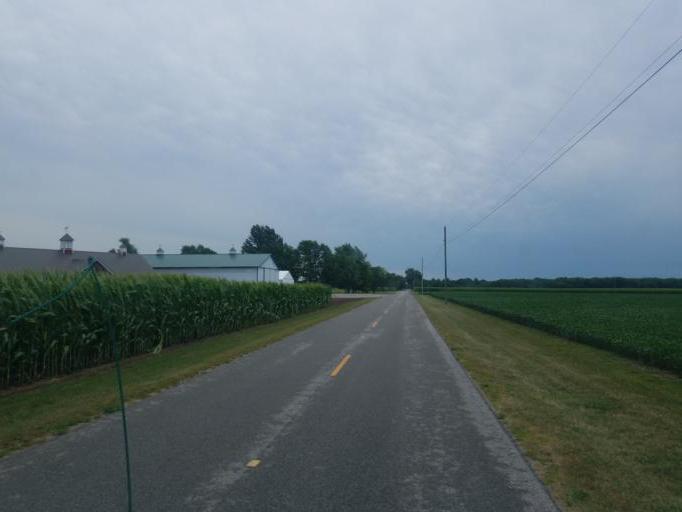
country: US
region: Ohio
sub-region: Paulding County
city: Antwerp
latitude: 41.2373
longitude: -84.7309
